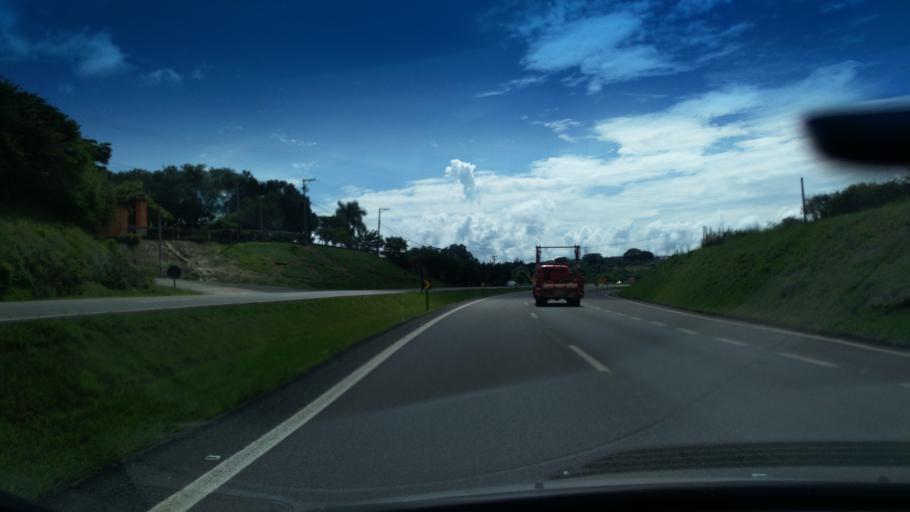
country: BR
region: Sao Paulo
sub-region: Santo Antonio Do Jardim
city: Espirito Santo do Pinhal
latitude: -22.1993
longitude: -46.7774
